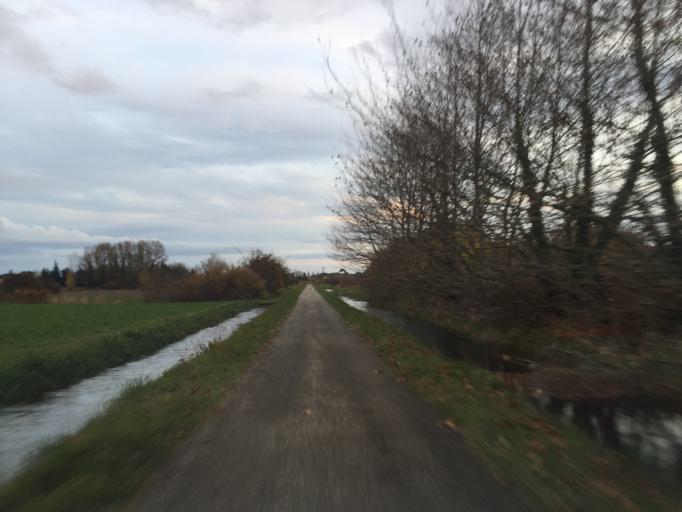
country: FR
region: Provence-Alpes-Cote d'Azur
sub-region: Departement du Vaucluse
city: Courthezon
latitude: 44.0857
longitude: 4.8664
